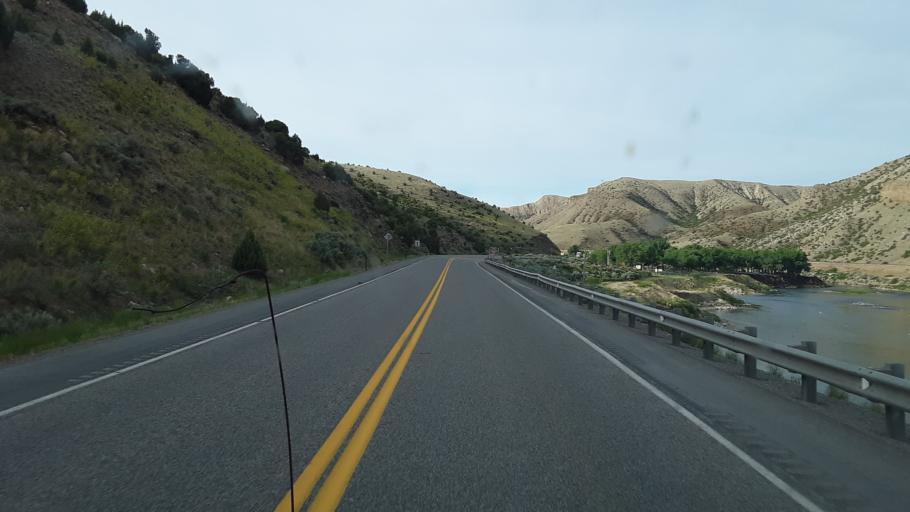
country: US
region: Wyoming
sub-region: Hot Springs County
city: Thermopolis
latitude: 43.4366
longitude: -108.1759
